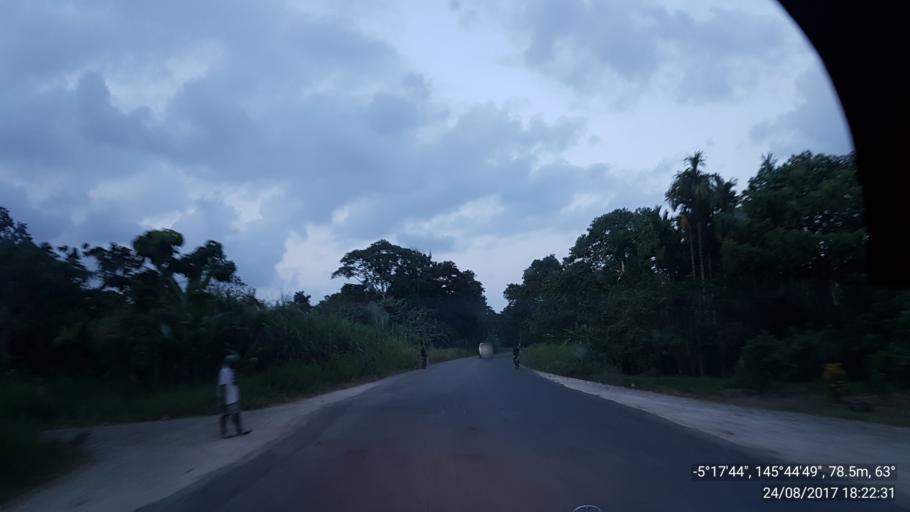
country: PG
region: Madang
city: Madang
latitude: -5.2956
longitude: 145.7469
